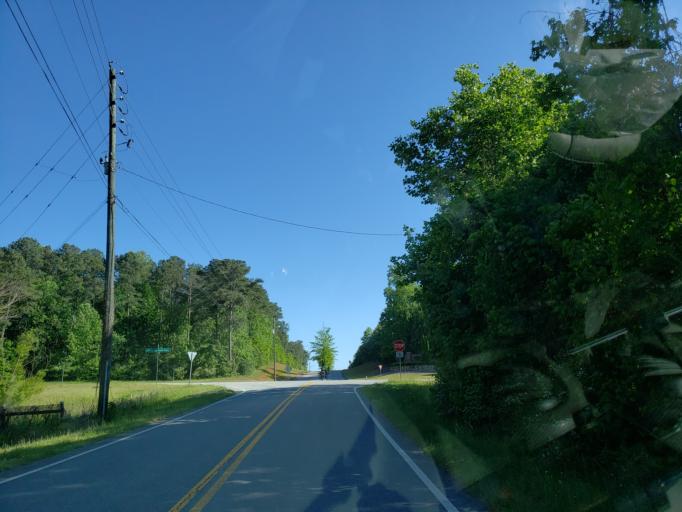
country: US
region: Georgia
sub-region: Paulding County
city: Hiram
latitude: 33.9032
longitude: -84.7936
